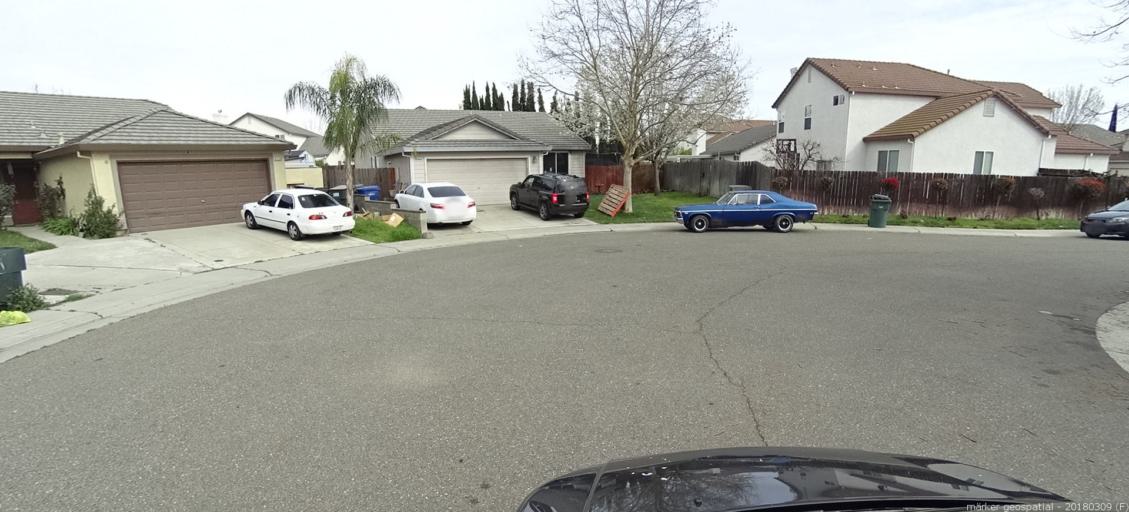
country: US
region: California
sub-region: Sacramento County
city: Vineyard
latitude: 38.4595
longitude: -121.3693
